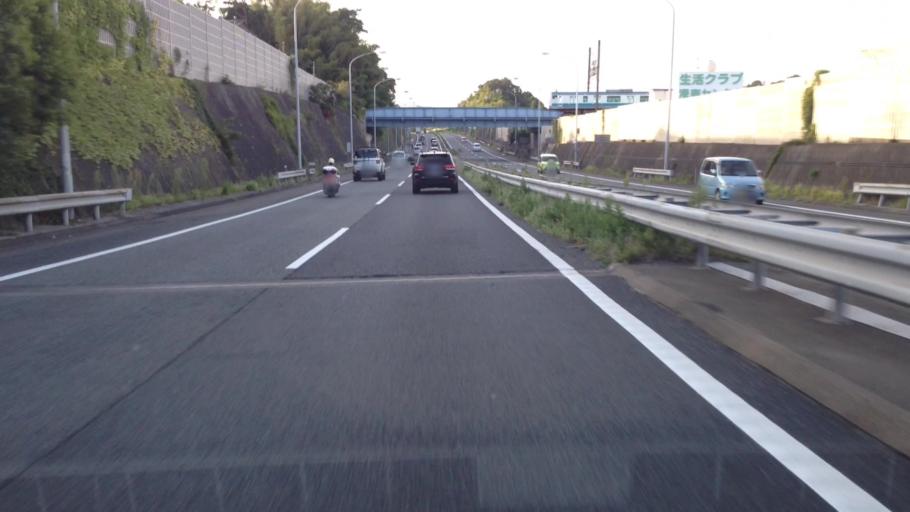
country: JP
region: Kanagawa
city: Kamakura
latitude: 35.3748
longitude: 139.5894
